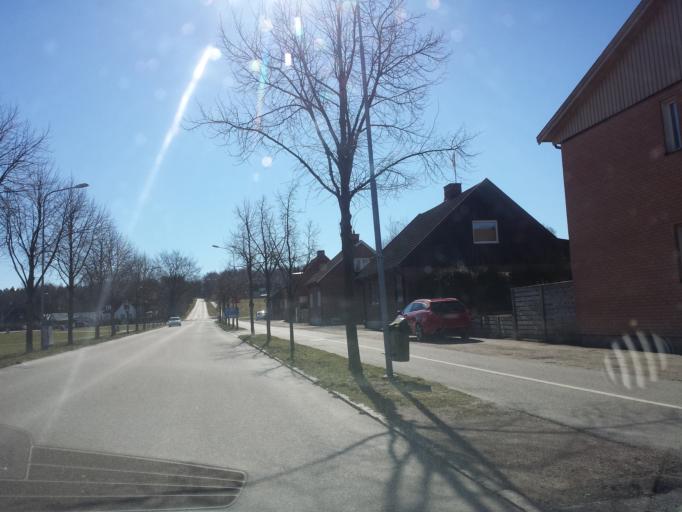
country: SE
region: Skane
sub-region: Sjobo Kommun
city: Sjoebo
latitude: 55.6295
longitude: 13.7104
